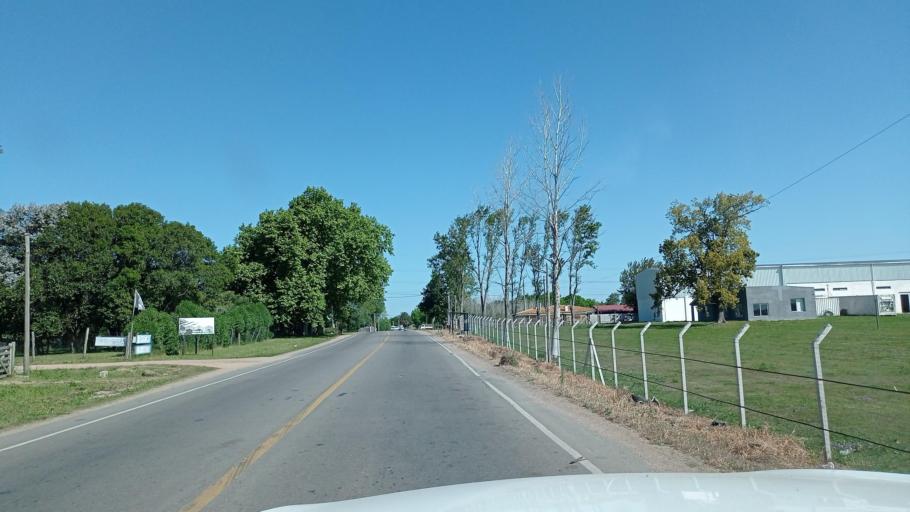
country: UY
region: Canelones
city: La Paz
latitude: -34.7841
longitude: -56.1678
